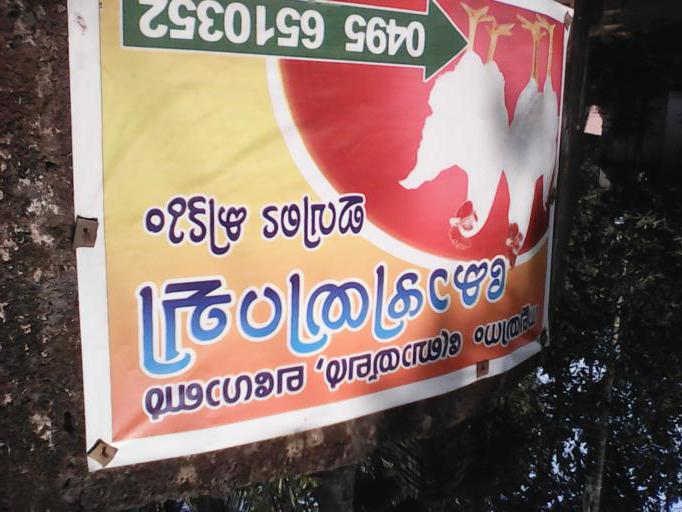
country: IN
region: Kerala
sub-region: Kozhikode
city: Kozhikode
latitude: 11.2796
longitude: 75.8106
